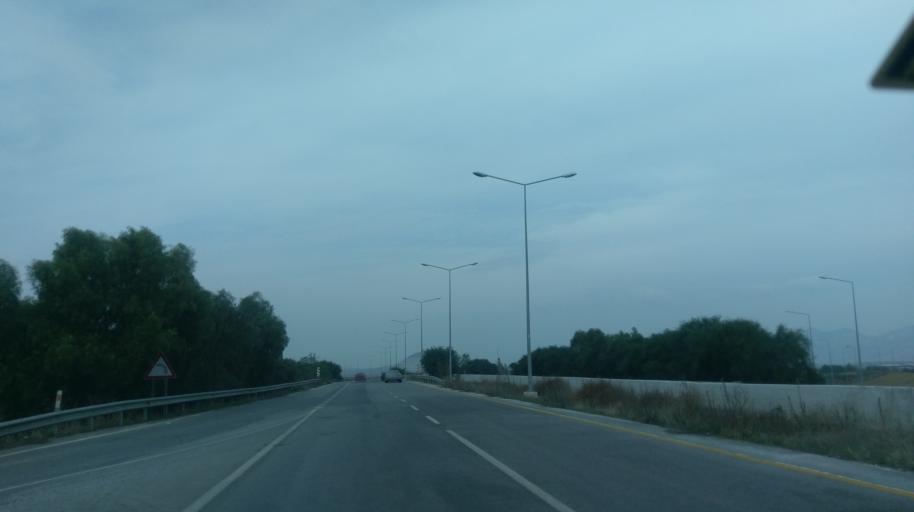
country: CY
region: Lefkosia
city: Mammari
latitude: 35.2167
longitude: 33.1803
